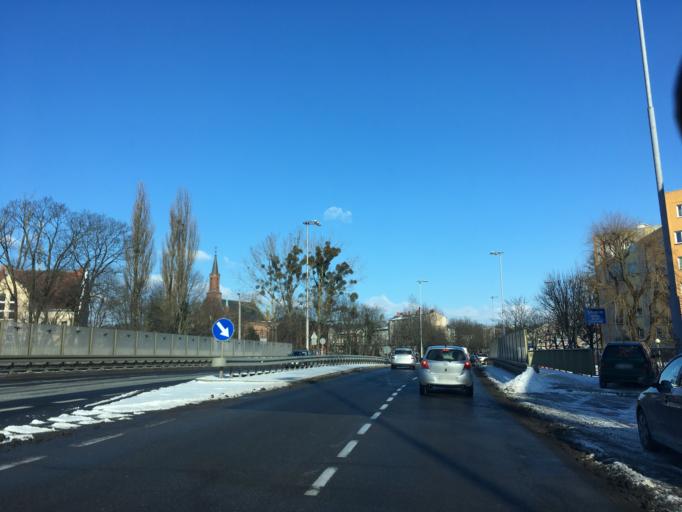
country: PL
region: Pomeranian Voivodeship
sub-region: Slupsk
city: Slupsk
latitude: 54.4644
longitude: 17.0358
